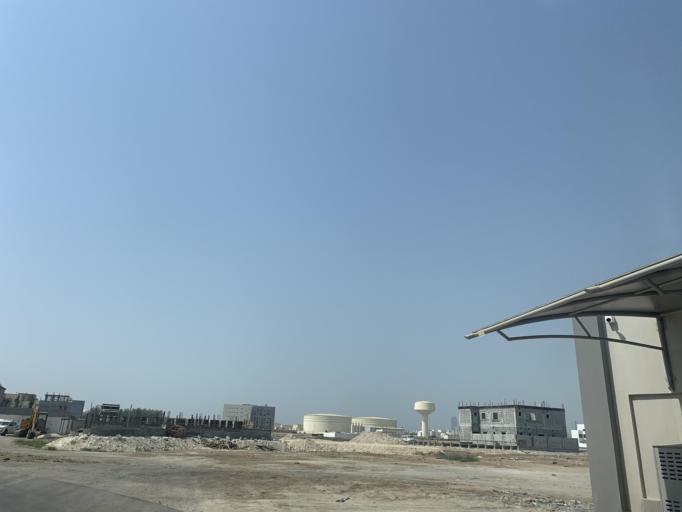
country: BH
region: Manama
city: Jidd Hafs
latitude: 26.2025
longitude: 50.5244
